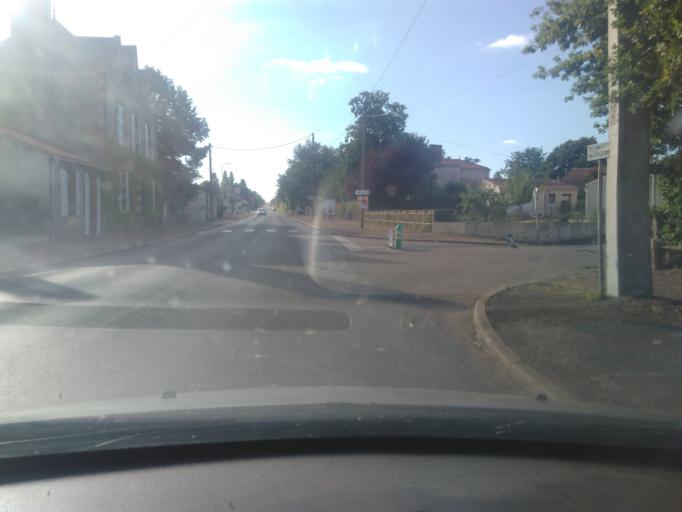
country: FR
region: Pays de la Loire
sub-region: Departement de la Vendee
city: Saint-Florent-des-Bois
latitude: 46.5951
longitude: -1.3183
